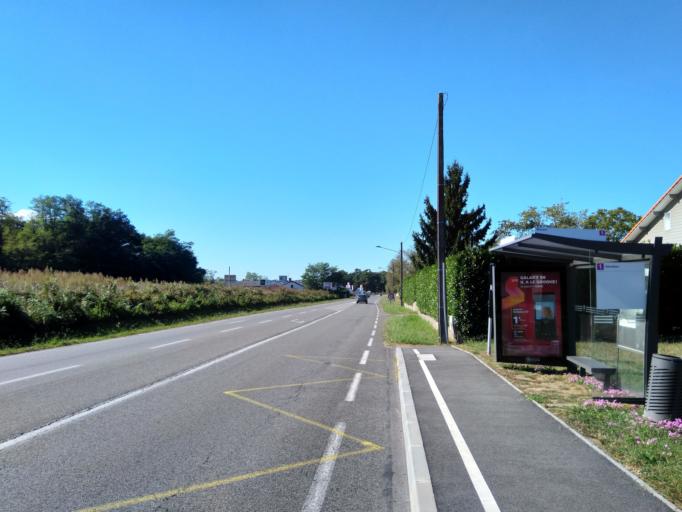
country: FR
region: Aquitaine
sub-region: Departement des Landes
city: Narrosse
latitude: 43.6991
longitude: -1.0255
